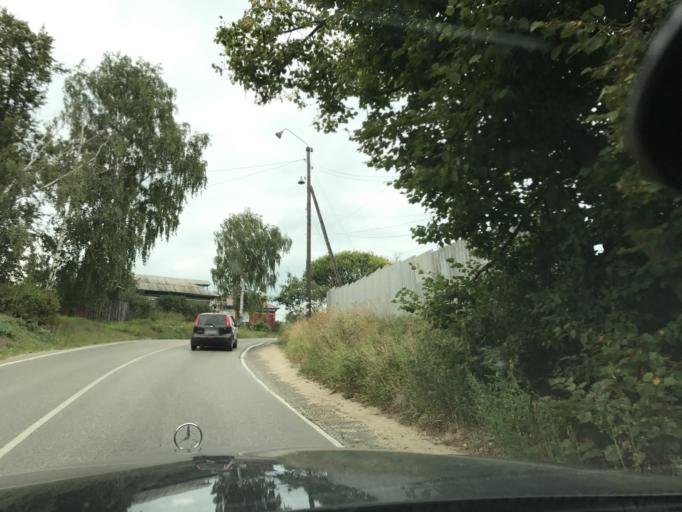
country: RU
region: Nizjnij Novgorod
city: Pavlovo
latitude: 55.9938
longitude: 43.0433
